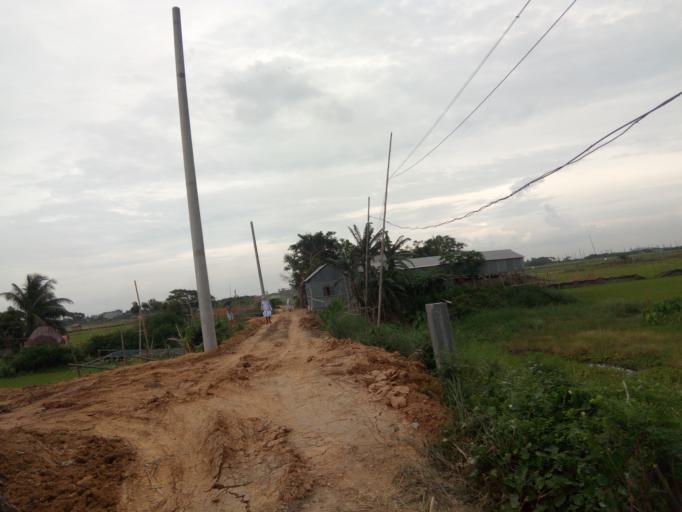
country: BD
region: Dhaka
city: Paltan
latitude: 23.7388
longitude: 90.4684
